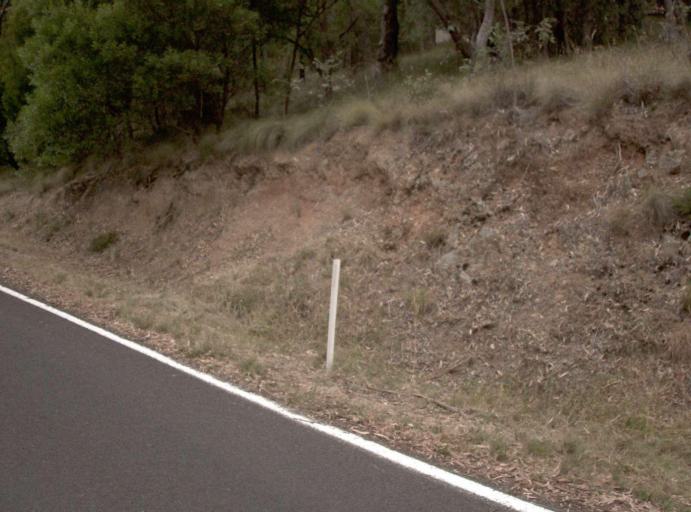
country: AU
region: Victoria
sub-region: Yarra Ranges
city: Badger Creek
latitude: -37.6918
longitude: 145.5506
